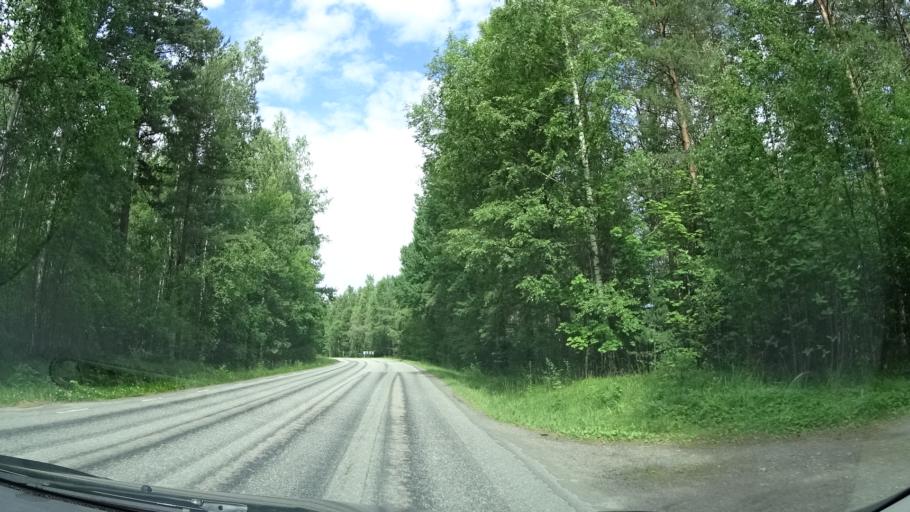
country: SE
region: Vaestmanland
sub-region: Vasteras
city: Tillberga
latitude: 59.6460
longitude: 16.6160
